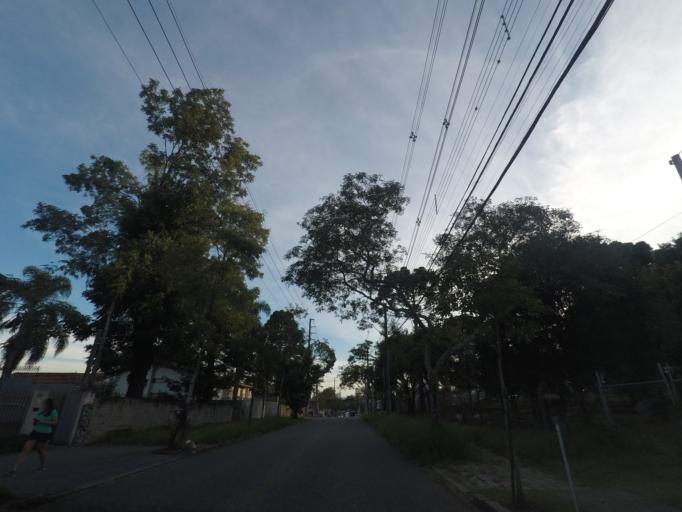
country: BR
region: Parana
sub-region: Curitiba
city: Curitiba
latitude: -25.4164
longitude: -49.2496
